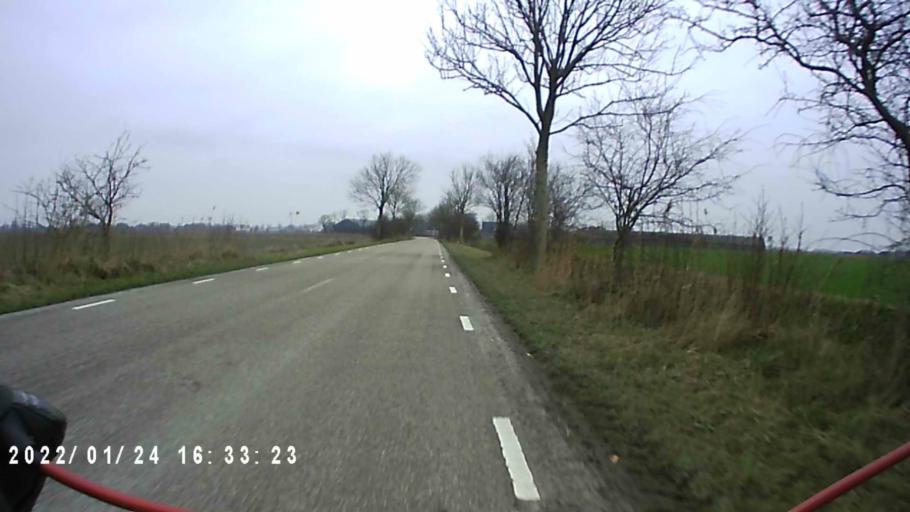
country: NL
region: Groningen
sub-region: Gemeente Zuidhorn
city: Oldehove
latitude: 53.3747
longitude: 6.4205
